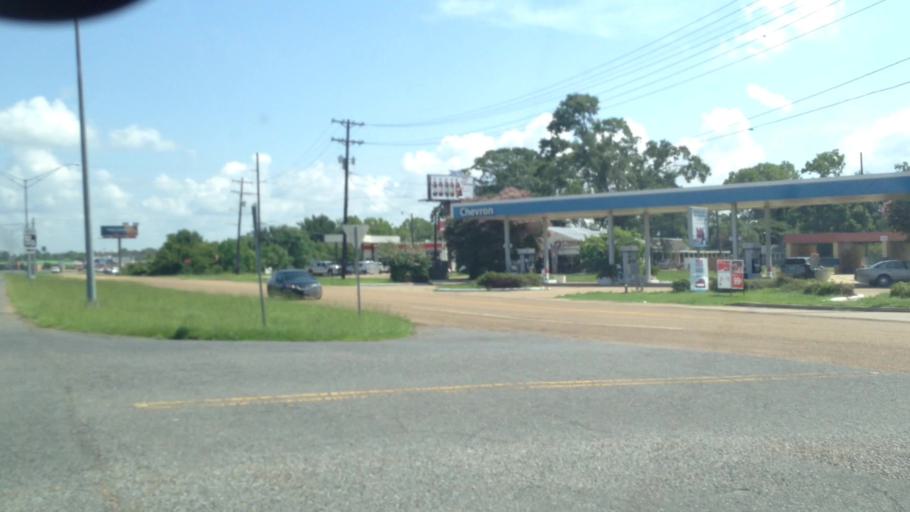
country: US
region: Louisiana
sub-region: Rapides Parish
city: Alexandria
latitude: 31.3040
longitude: -92.4798
